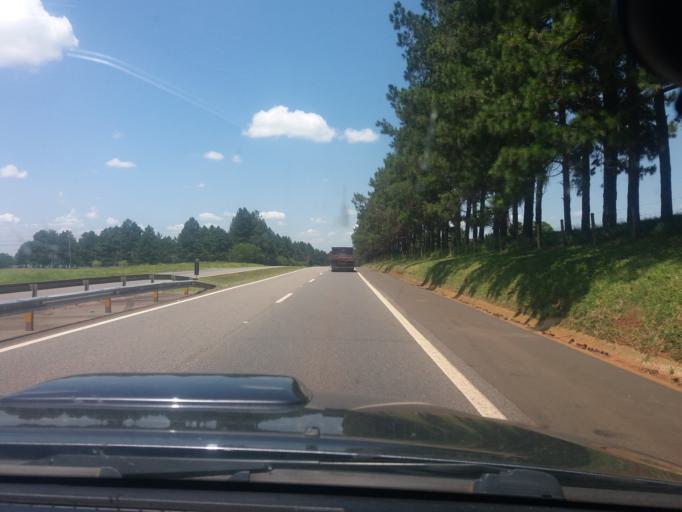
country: BR
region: Sao Paulo
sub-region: Tatui
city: Tatui
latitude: -23.3627
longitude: -47.8987
